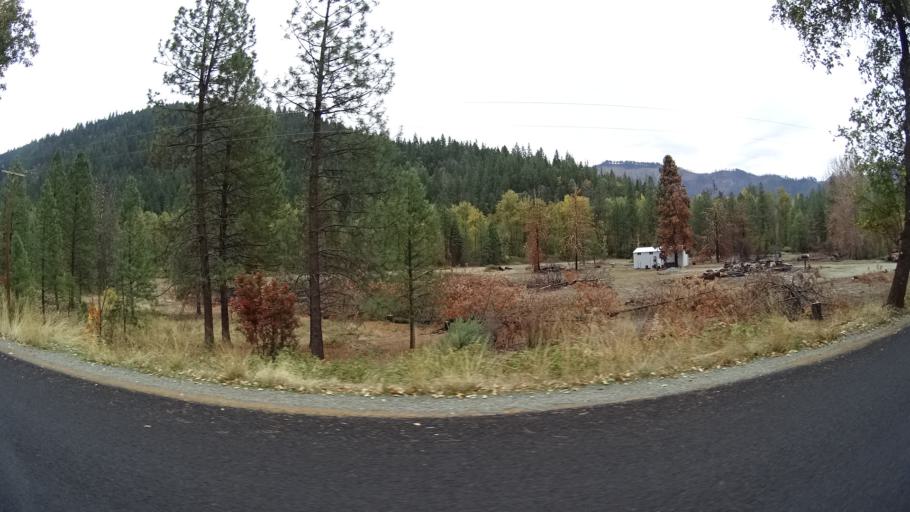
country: US
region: California
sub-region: Siskiyou County
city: Happy Camp
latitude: 41.8479
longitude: -123.1847
